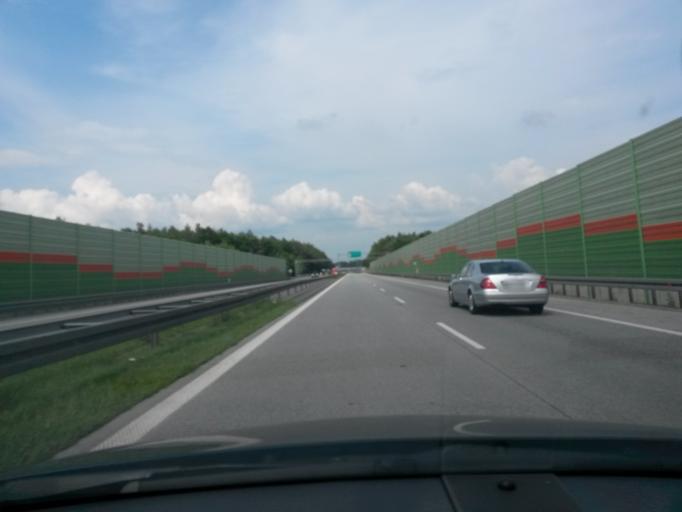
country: PL
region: Lodz Voivodeship
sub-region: Powiat tomaszowski
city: Tomaszow Mazowiecki
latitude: 51.5593
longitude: 20.0107
